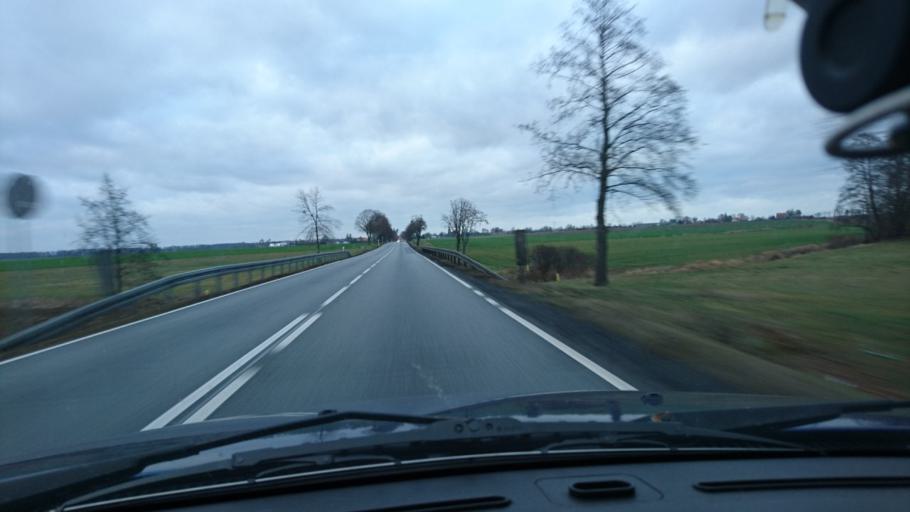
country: PL
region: Opole Voivodeship
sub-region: Powiat kluczborski
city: Kluczbork
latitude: 51.0168
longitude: 18.1992
